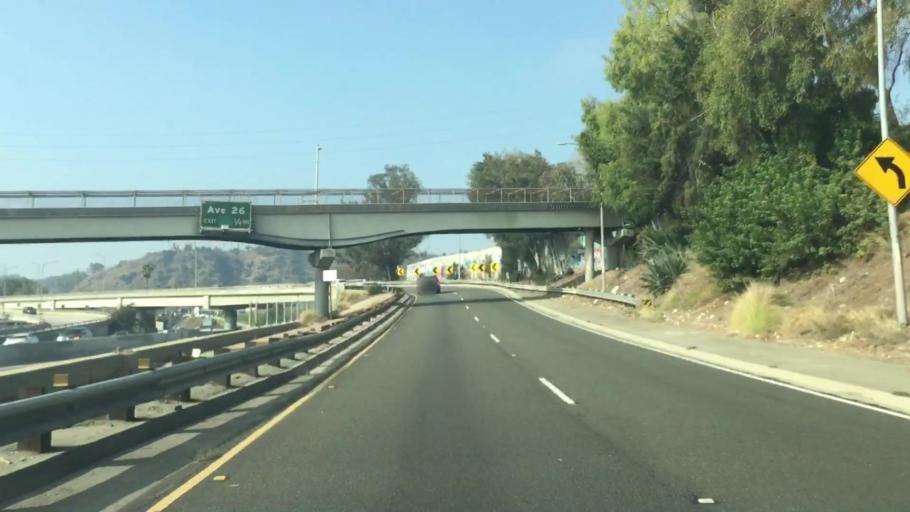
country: US
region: California
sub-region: Los Angeles County
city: Los Angeles
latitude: 34.0857
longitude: -118.2172
